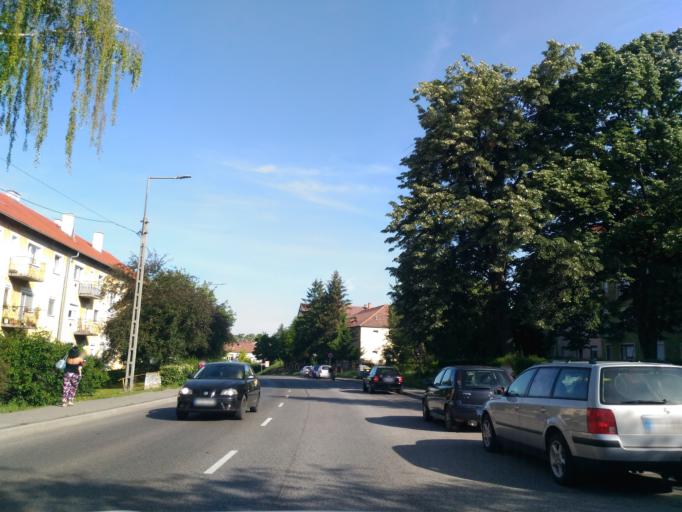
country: HU
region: Baranya
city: Komlo
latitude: 46.1838
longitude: 18.2587
